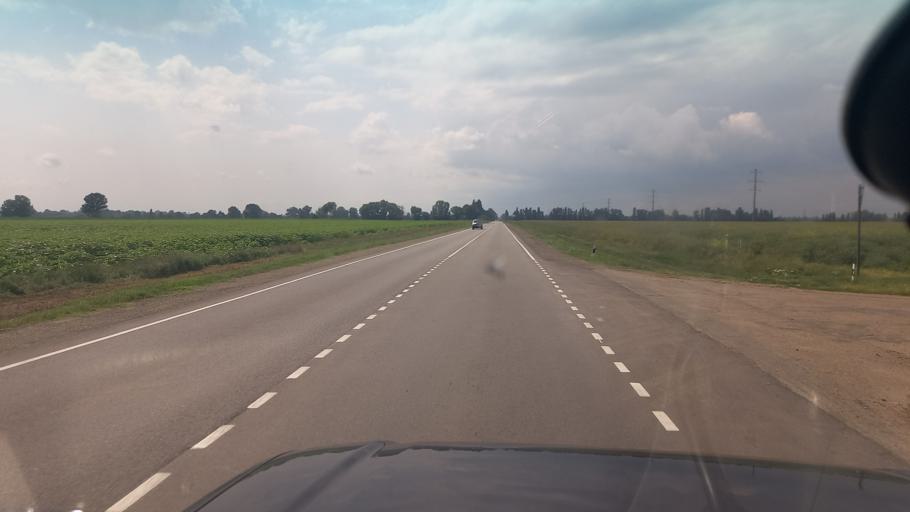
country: RU
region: Adygeya
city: Koshekhabl'
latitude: 44.9080
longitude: 40.4579
